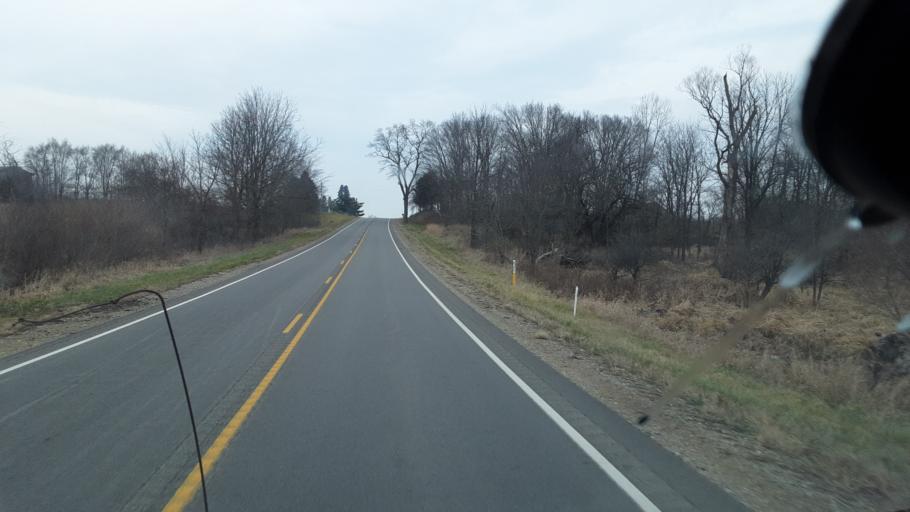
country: US
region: Indiana
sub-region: Steuben County
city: Angola
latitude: 41.6149
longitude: -85.1696
